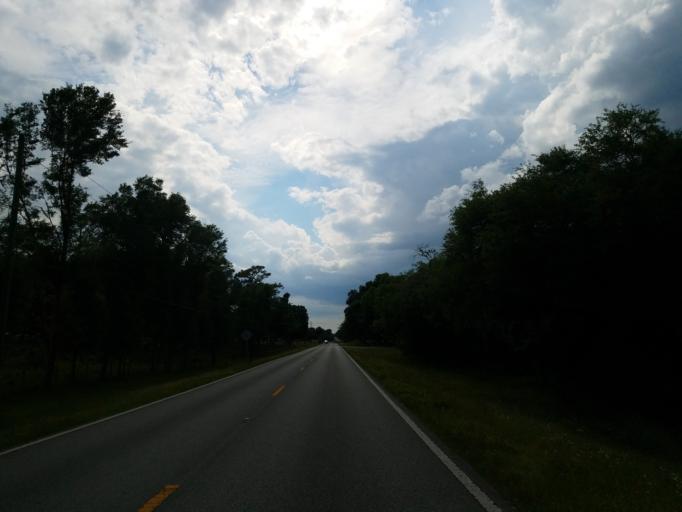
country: US
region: Florida
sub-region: Hernando County
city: Hill 'n Dale
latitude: 28.5534
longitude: -82.3203
